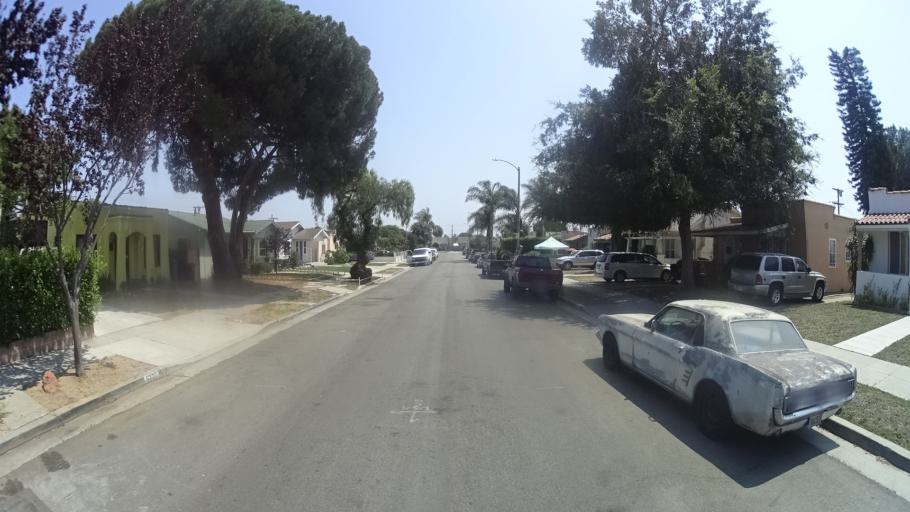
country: US
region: California
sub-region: Los Angeles County
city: View Park-Windsor Hills
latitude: 33.9830
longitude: -118.3409
